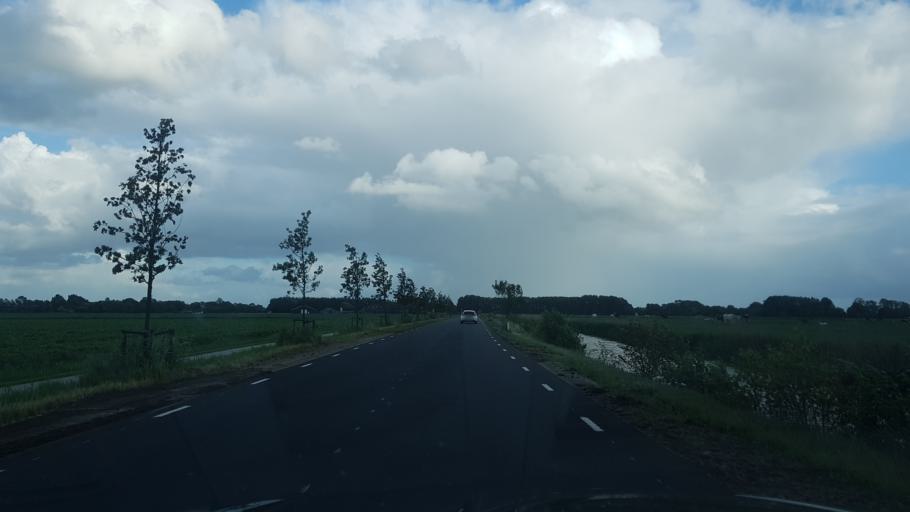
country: NL
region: Groningen
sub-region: Gemeente Appingedam
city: Appingedam
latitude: 53.3198
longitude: 6.7635
